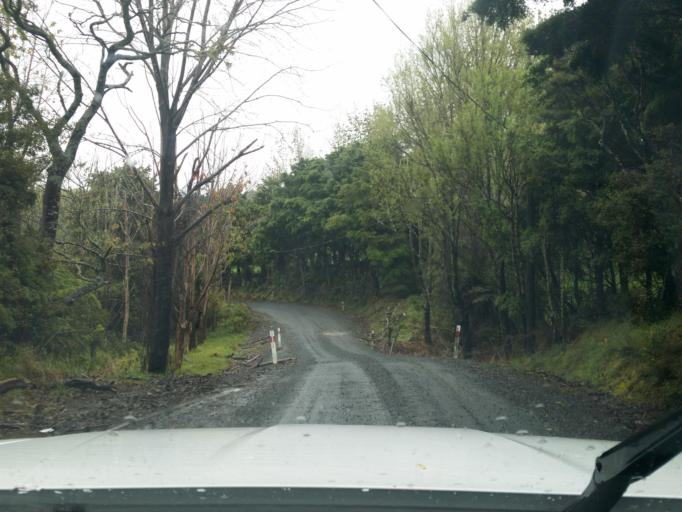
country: NZ
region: Northland
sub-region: Kaipara District
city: Dargaville
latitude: -35.7693
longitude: 173.9626
